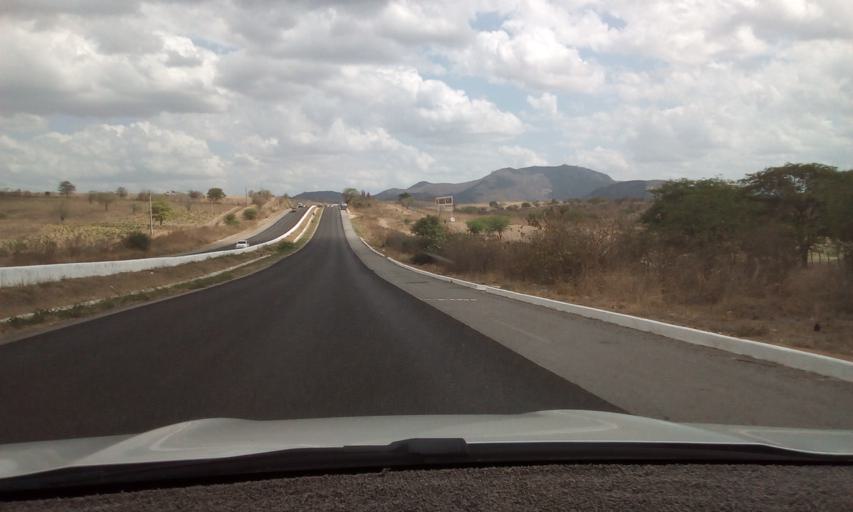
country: BR
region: Pernambuco
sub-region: Toritama
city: Toritama
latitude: -8.0451
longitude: -36.0506
